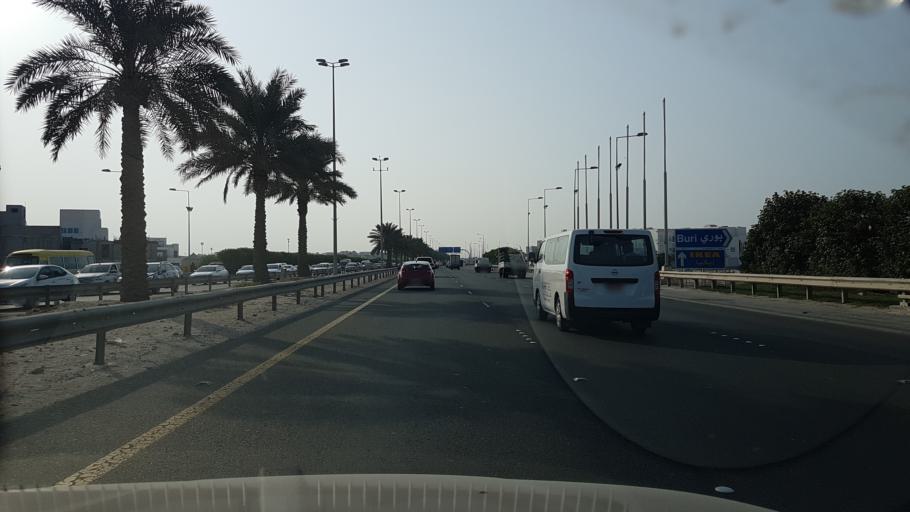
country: BH
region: Central Governorate
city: Madinat Hamad
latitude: 26.1530
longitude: 50.5074
